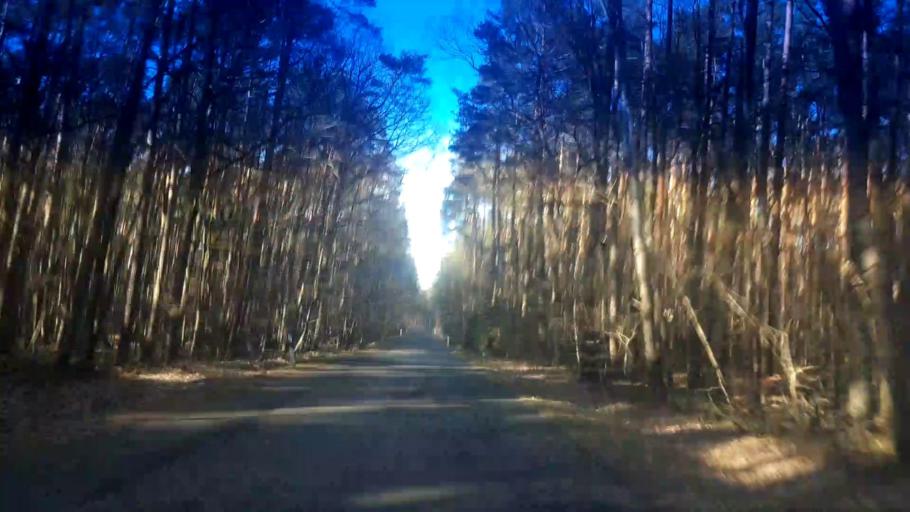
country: DE
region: Bavaria
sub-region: Upper Franconia
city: Lauter
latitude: 49.9591
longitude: 10.7617
